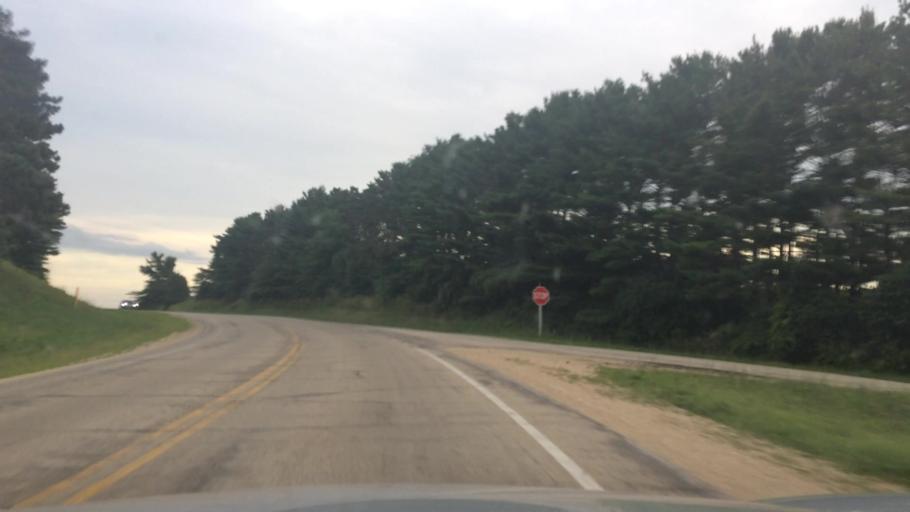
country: US
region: Wisconsin
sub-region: Columbia County
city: Lodi
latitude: 43.2346
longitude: -89.5407
